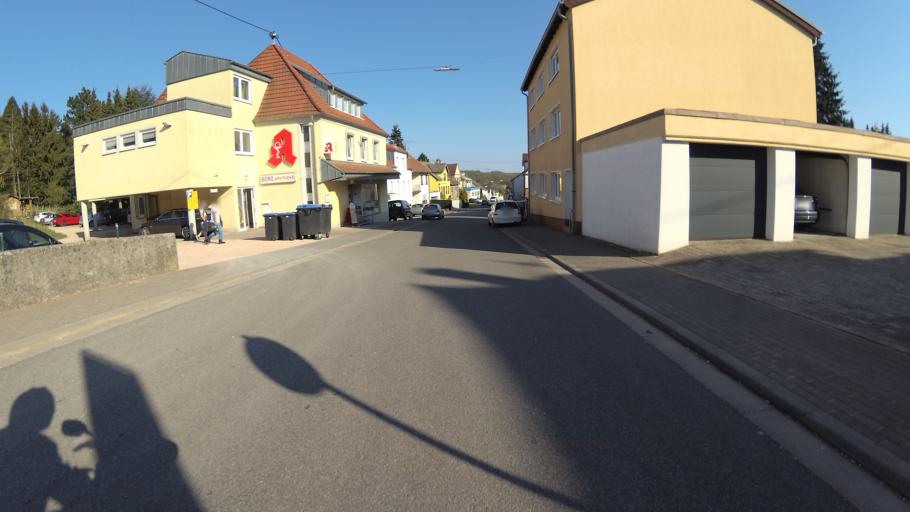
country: DE
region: Saarland
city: Merchweiler
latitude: 49.3588
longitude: 7.0585
